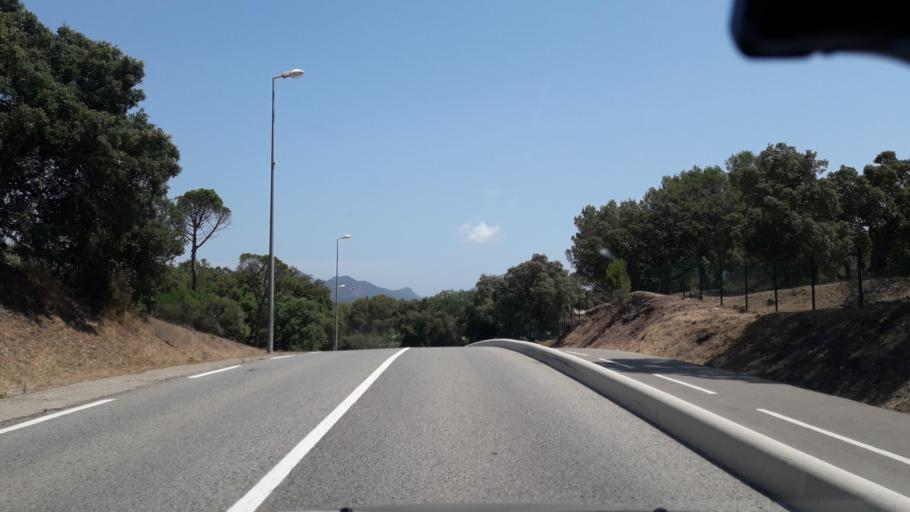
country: FR
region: Provence-Alpes-Cote d'Azur
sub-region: Departement du Var
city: Saint-Raphael
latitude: 43.4477
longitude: 6.8142
